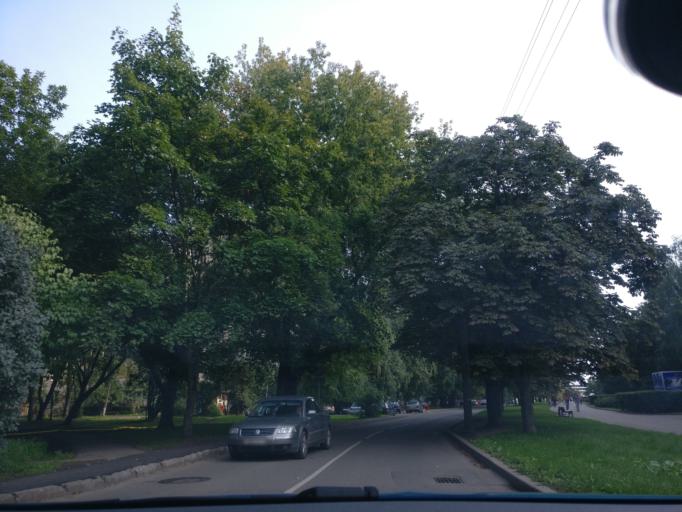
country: BY
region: Minsk
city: Minsk
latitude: 53.9258
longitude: 27.5743
